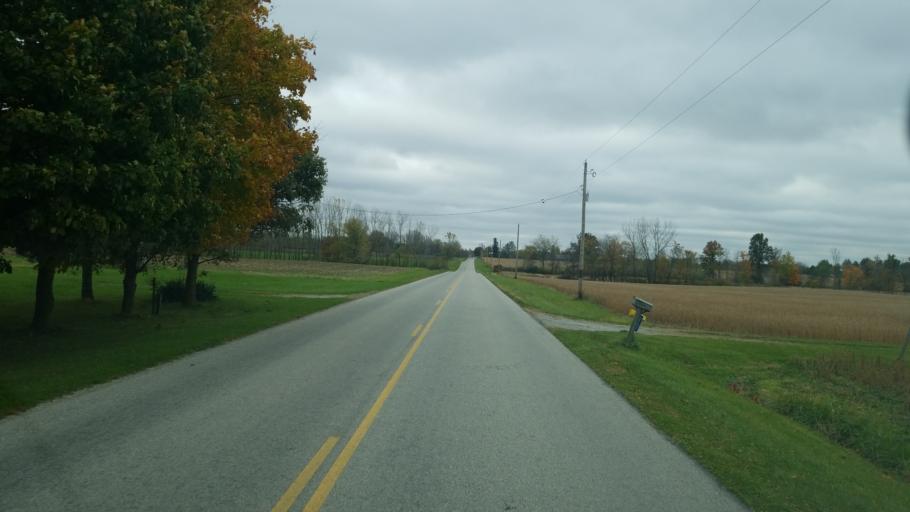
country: US
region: Ohio
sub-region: Seneca County
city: Tiffin
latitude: 41.0714
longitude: -82.9962
